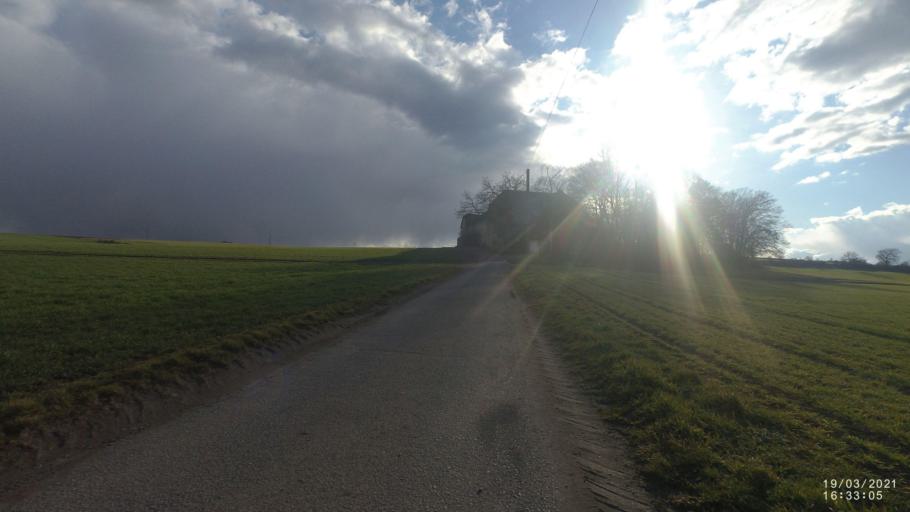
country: DE
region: Rheinland-Pfalz
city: Welling
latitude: 50.3530
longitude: 7.3147
